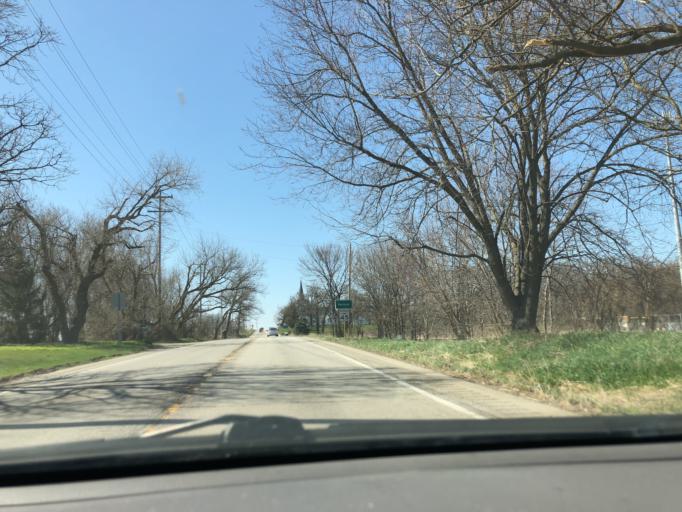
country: US
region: Illinois
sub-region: Kane County
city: Hampshire
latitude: 42.1573
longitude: -88.5224
